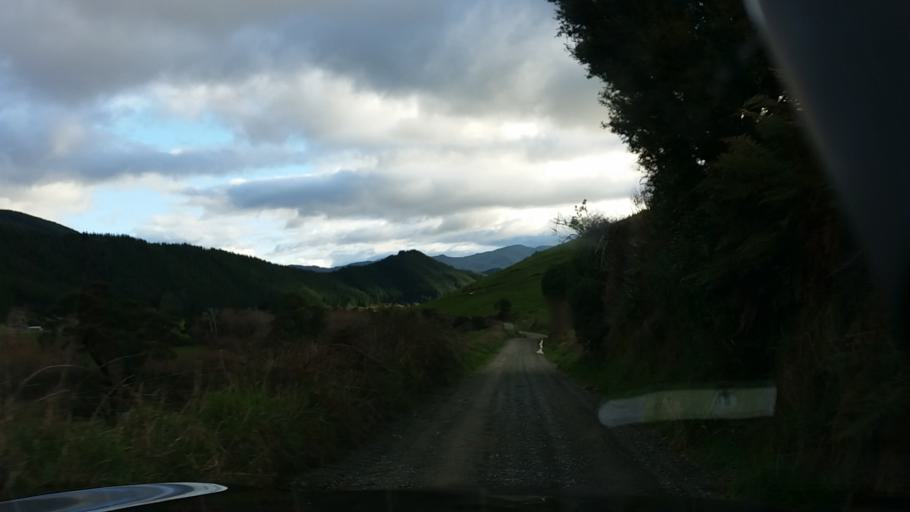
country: NZ
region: Nelson
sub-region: Nelson City
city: Nelson
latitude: -41.2081
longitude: 173.6365
